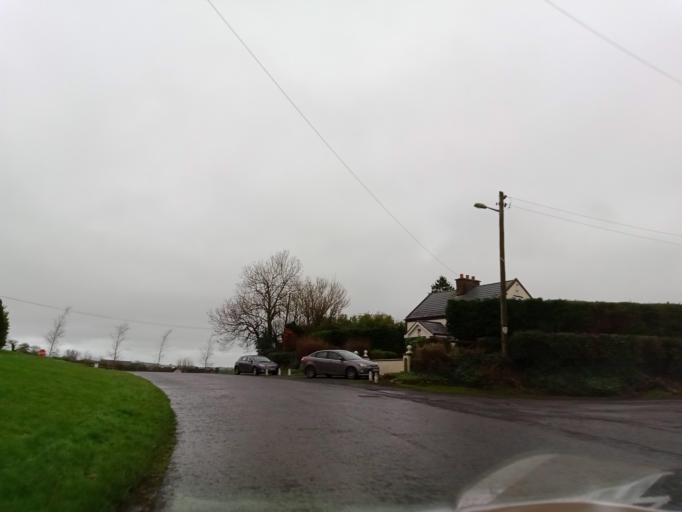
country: IE
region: Munster
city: Fethard
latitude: 52.5655
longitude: -7.6788
